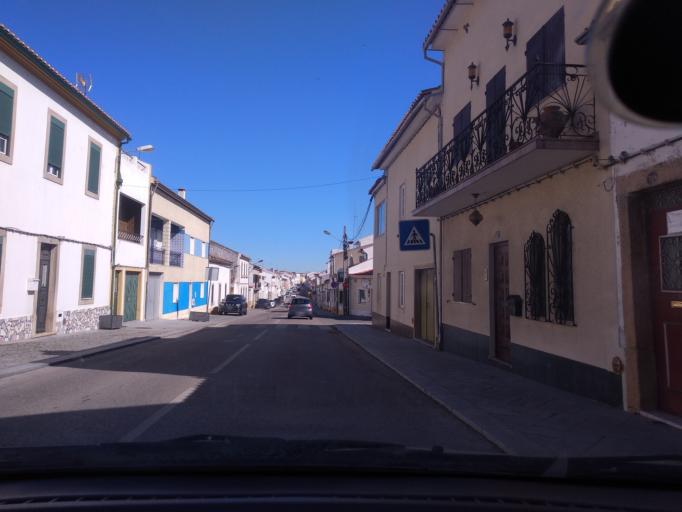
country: PT
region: Portalegre
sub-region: Nisa
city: Nisa
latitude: 39.5102
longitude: -7.6465
